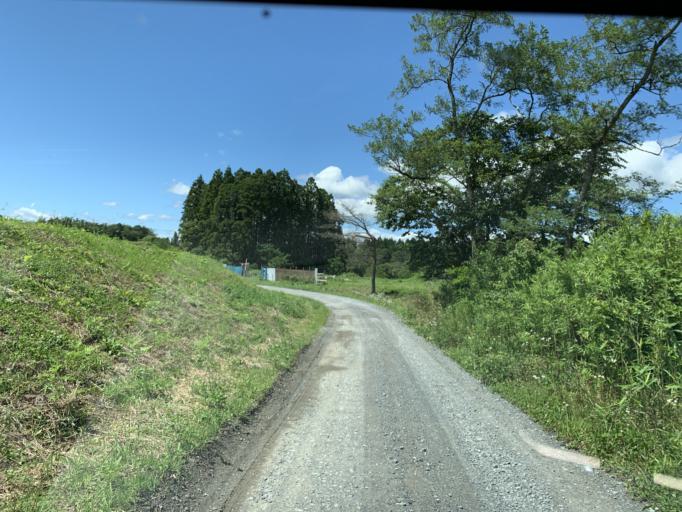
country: JP
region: Iwate
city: Ichinoseki
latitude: 38.9236
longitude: 141.0605
